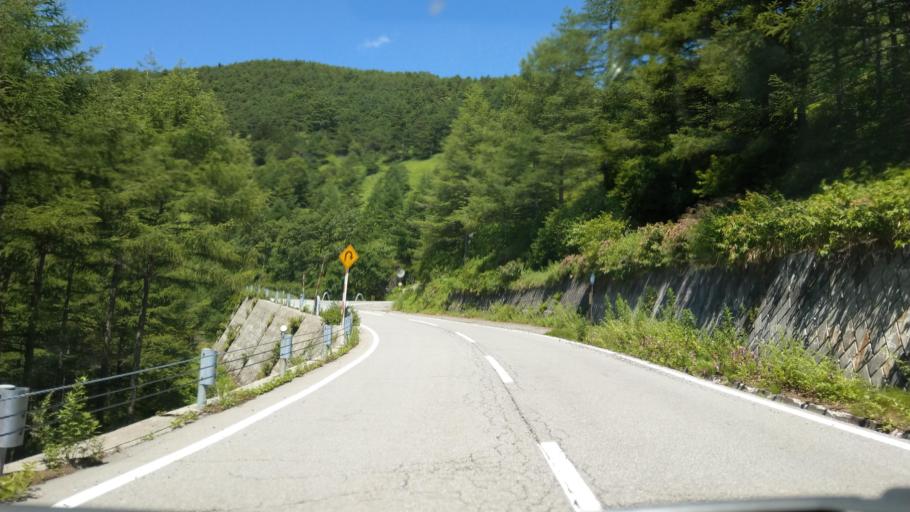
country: JP
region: Nagano
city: Komoro
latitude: 36.4018
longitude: 138.4702
